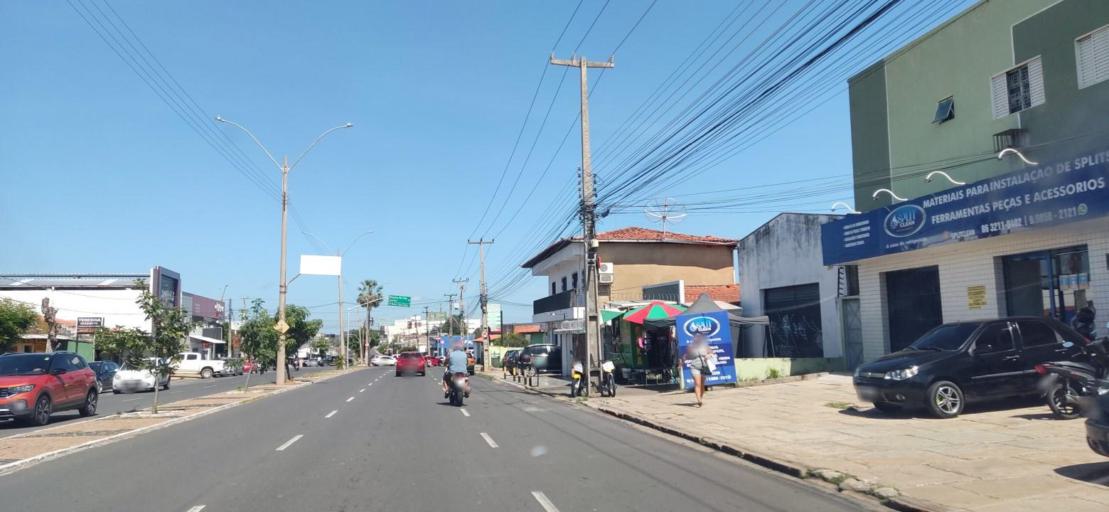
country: BR
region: Piaui
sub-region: Teresina
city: Teresina
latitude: -5.1119
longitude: -42.8010
